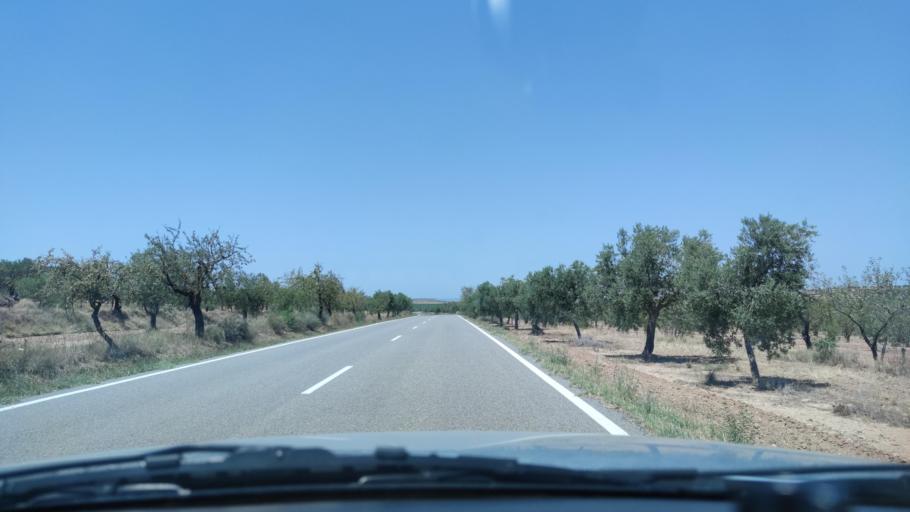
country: ES
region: Catalonia
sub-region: Provincia de Lleida
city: Alcano
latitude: 41.4479
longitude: 0.6387
